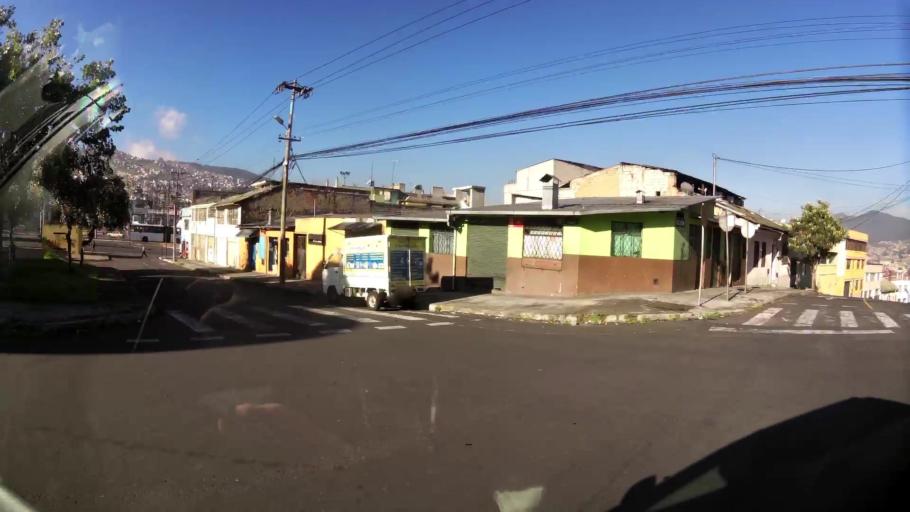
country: EC
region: Pichincha
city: Quito
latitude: -0.2447
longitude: -78.5159
